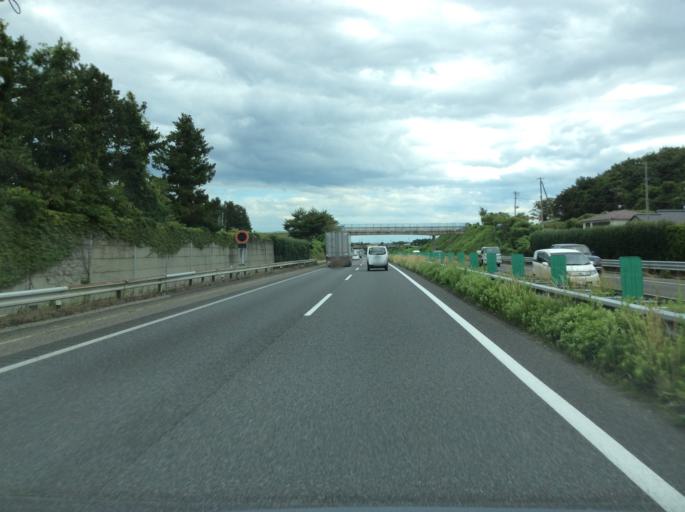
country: JP
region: Fukushima
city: Motomiya
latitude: 37.5111
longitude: 140.3809
